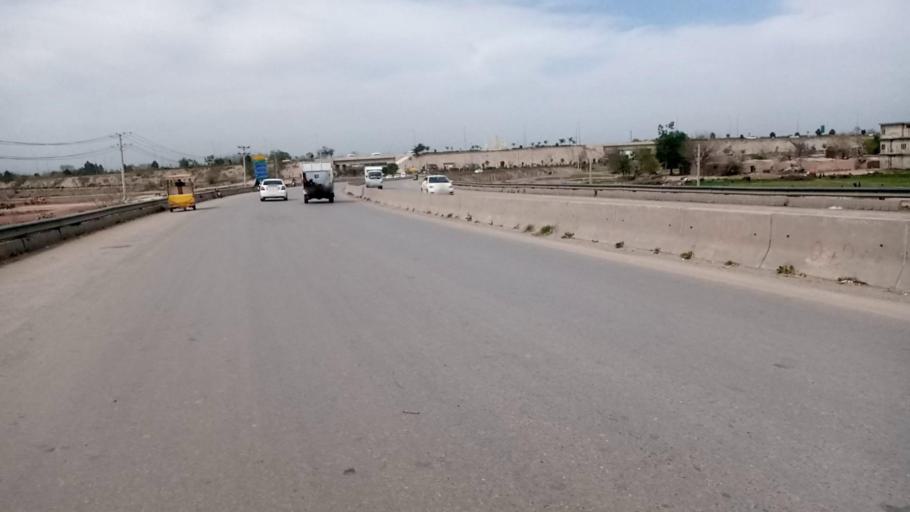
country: PK
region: Khyber Pakhtunkhwa
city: Peshawar
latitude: 34.0231
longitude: 71.6450
